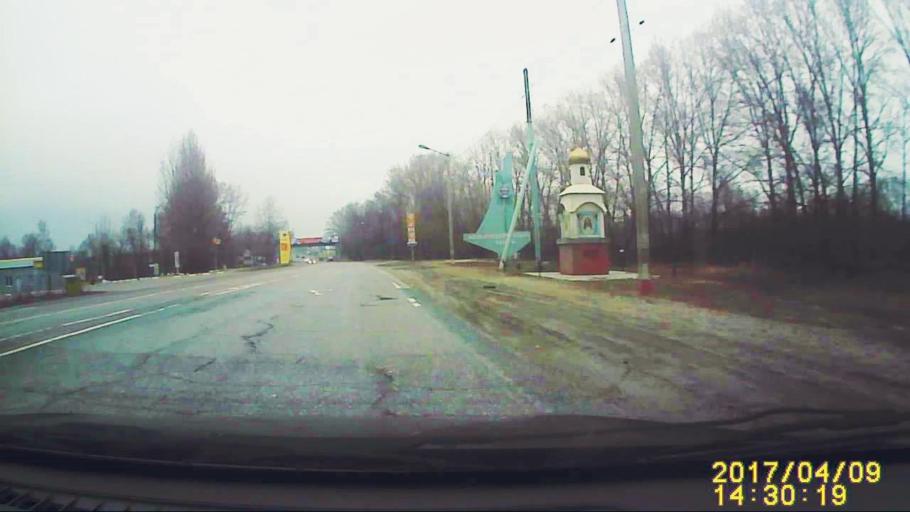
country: RU
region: Ulyanovsk
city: Novoul'yanovsk
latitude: 54.2126
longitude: 48.2972
